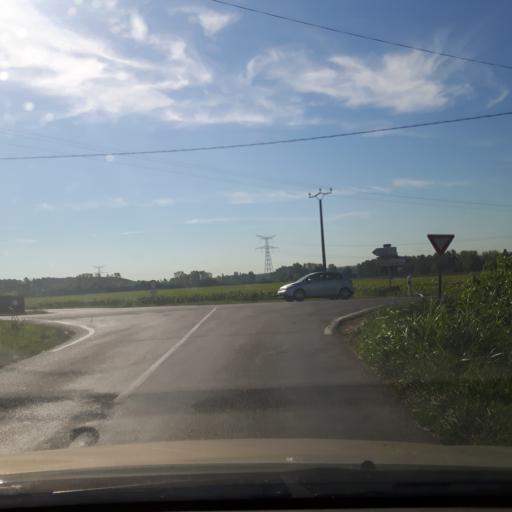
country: FR
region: Midi-Pyrenees
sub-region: Departement de la Haute-Garonne
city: Cepet
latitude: 43.7576
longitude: 1.4370
